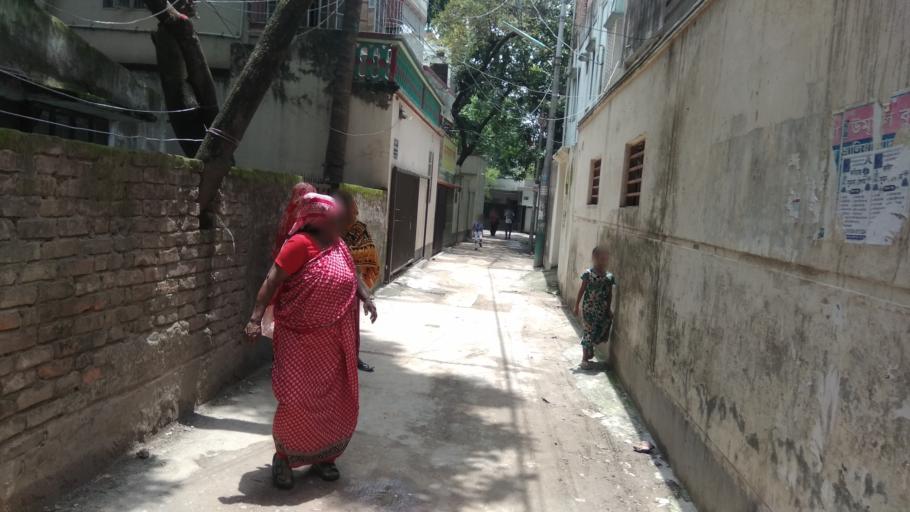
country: BD
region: Dhaka
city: Tungi
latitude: 23.8154
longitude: 90.3786
